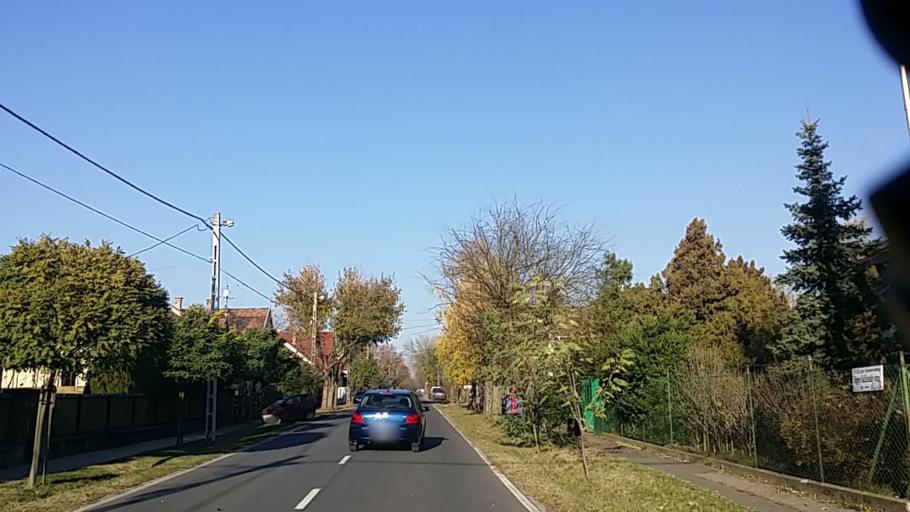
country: HU
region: Budapest
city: Budapest XVIII. keruelet
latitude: 47.4347
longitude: 19.2084
